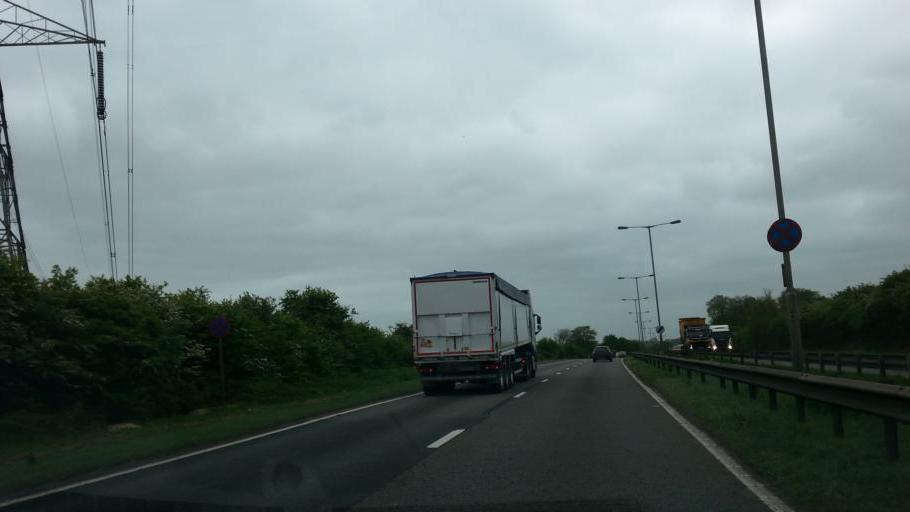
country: GB
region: England
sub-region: Lincolnshire
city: Grantham
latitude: 52.8714
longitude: -0.6303
